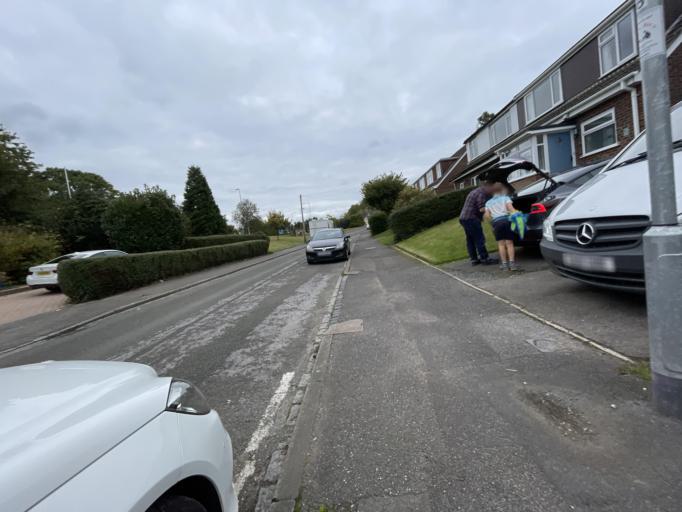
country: GB
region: England
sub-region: West Berkshire
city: Tilehurst
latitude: 51.4585
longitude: -1.0283
